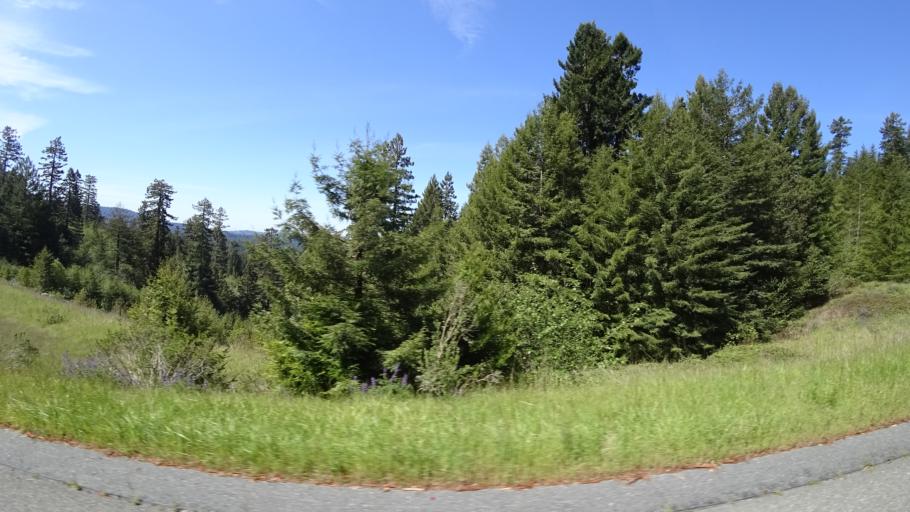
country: US
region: California
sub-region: Humboldt County
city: Westhaven-Moonstone
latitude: 41.3646
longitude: -123.9898
